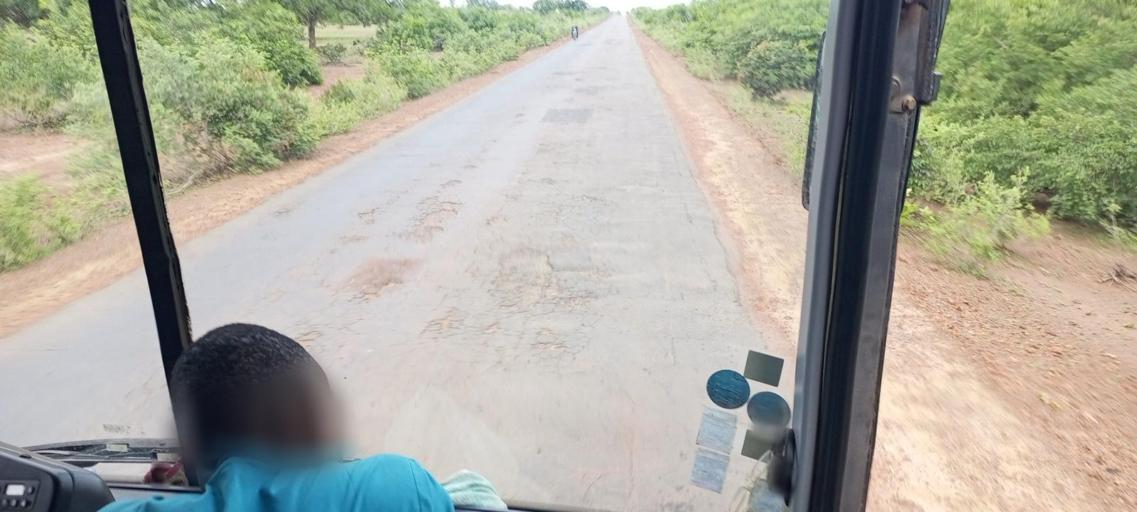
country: ML
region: Sikasso
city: Koutiala
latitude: 12.4867
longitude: -5.5339
